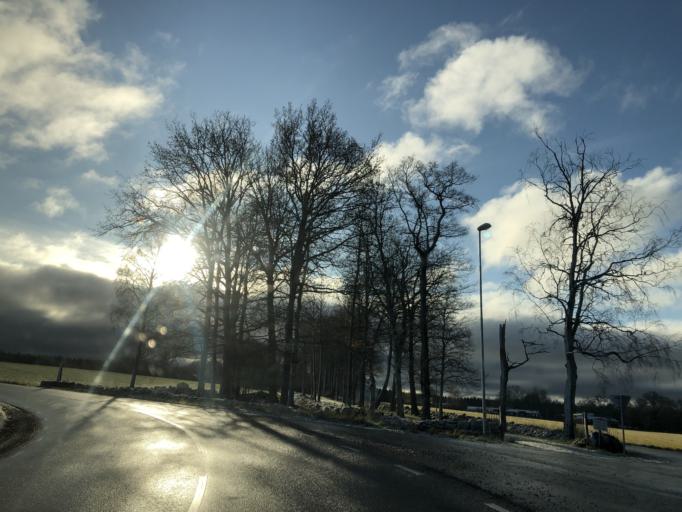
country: SE
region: Vaestra Goetaland
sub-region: Tranemo Kommun
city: Limmared
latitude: 57.6265
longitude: 13.4534
